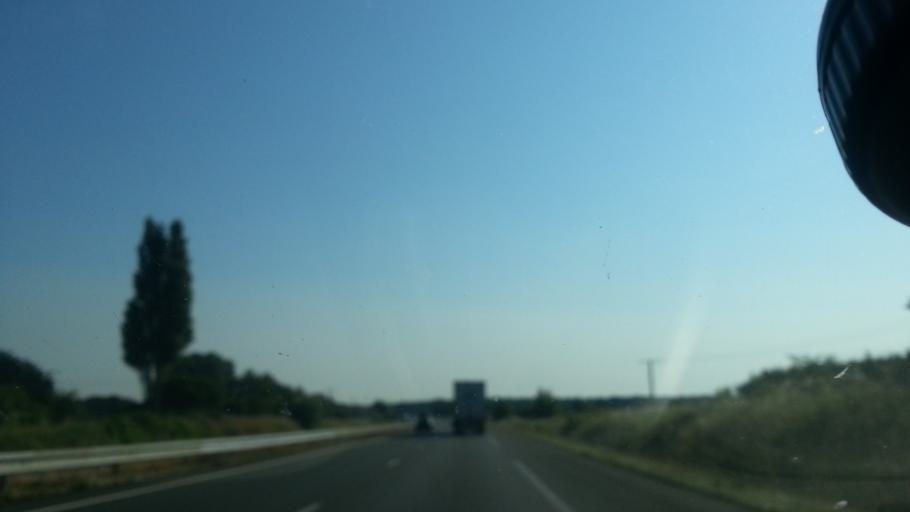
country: FR
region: Poitou-Charentes
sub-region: Departement de la Vienne
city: Naintre
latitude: 46.7716
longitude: 0.4844
